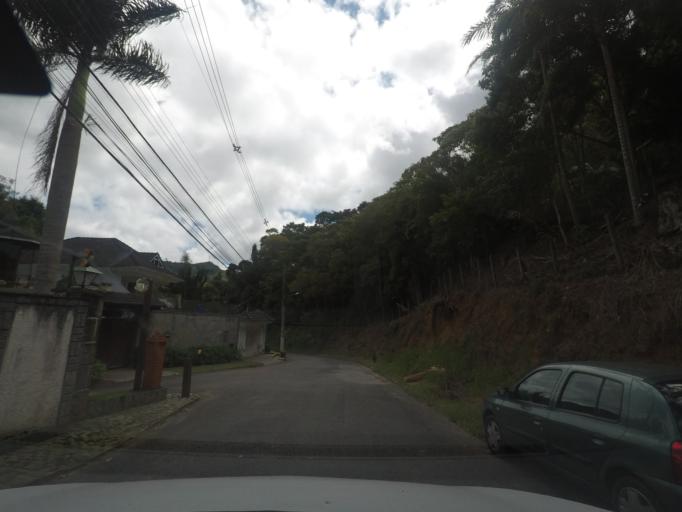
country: BR
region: Rio de Janeiro
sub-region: Teresopolis
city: Teresopolis
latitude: -22.4033
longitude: -42.9801
